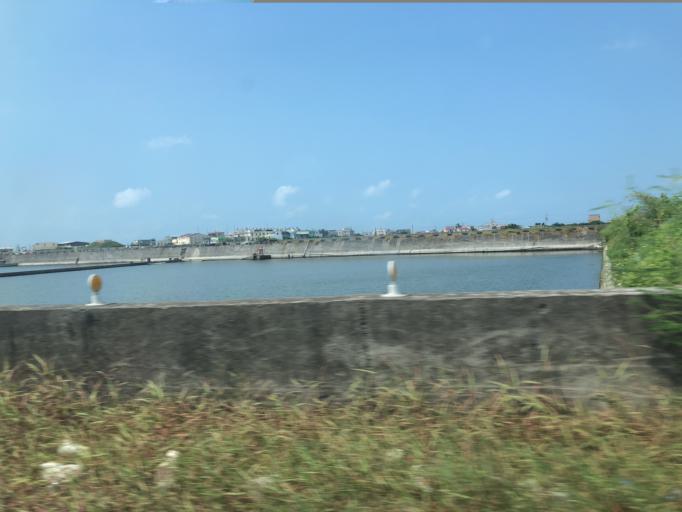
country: TW
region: Taiwan
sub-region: Chiayi
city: Taibao
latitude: 23.4686
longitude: 120.1524
